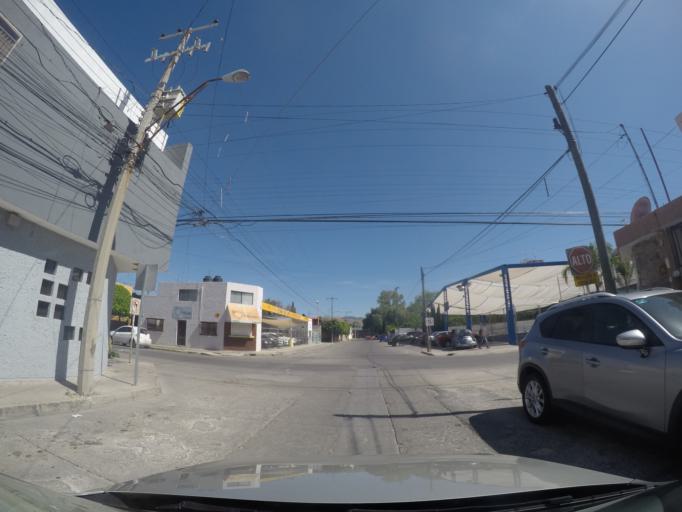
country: MX
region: San Luis Potosi
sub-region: San Luis Potosi
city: San Luis Potosi
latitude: 22.1509
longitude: -101.0068
